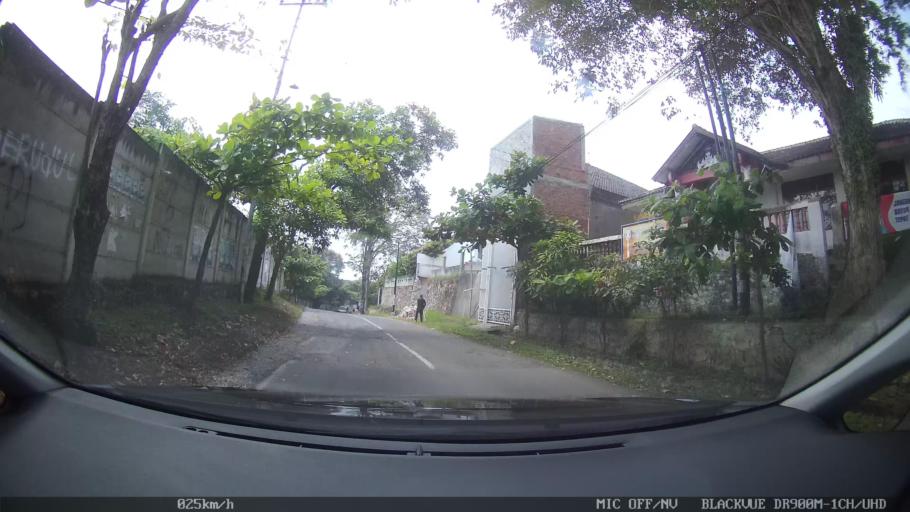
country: ID
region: Lampung
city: Bandarlampung
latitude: -5.4306
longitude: 105.2634
